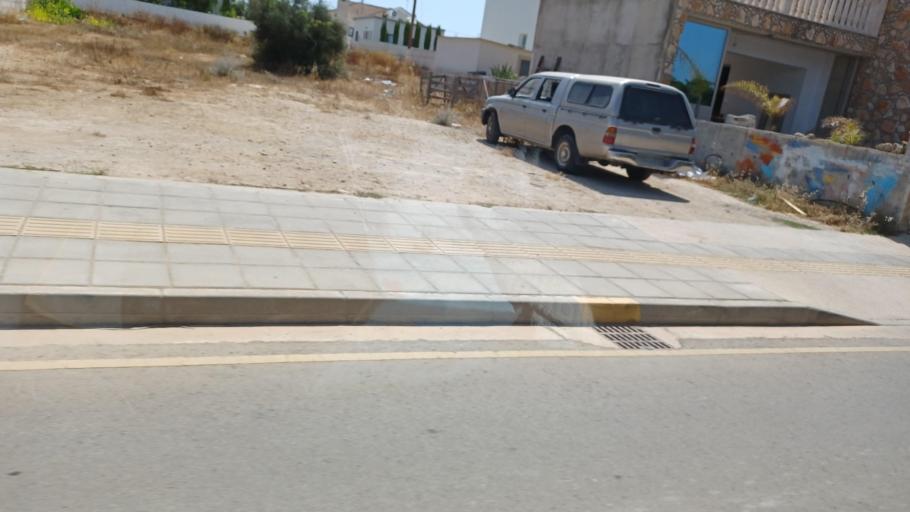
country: CY
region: Ammochostos
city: Paralimni
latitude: 35.0157
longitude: 33.9547
